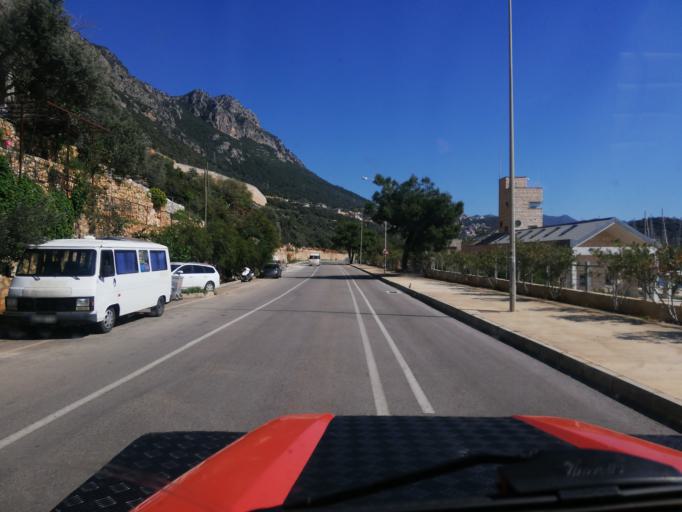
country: TR
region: Antalya
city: Kas
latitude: 36.2064
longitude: 29.6281
